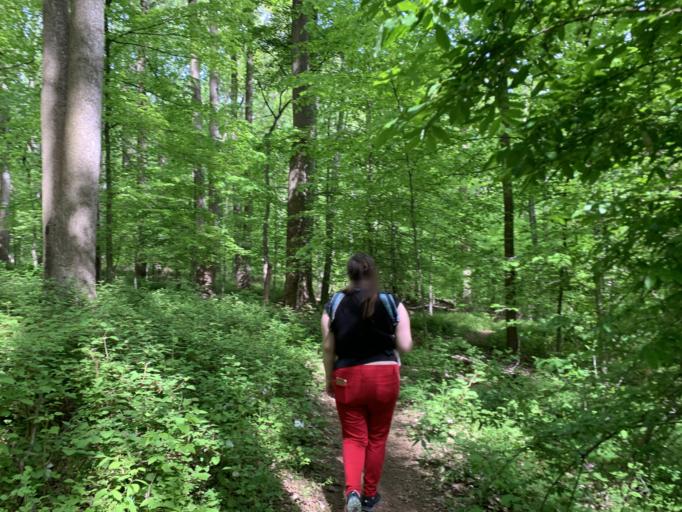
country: US
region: Maryland
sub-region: Harford County
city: South Bel Air
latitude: 39.6192
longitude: -76.2765
